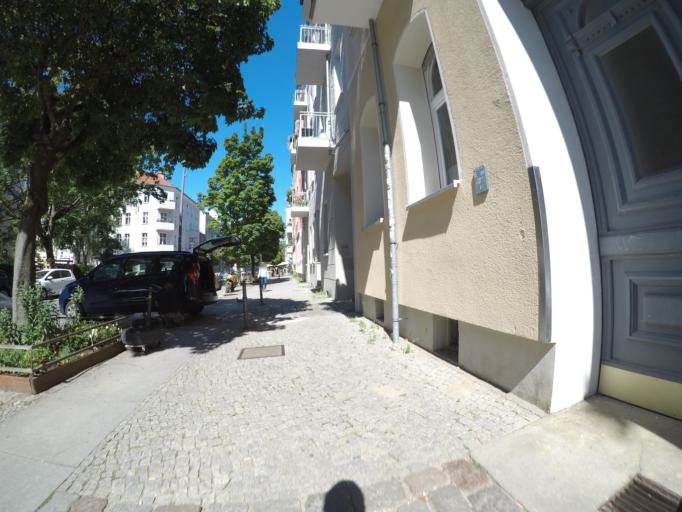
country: DE
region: Berlin
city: Rummelsburg
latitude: 52.5041
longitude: 13.4807
